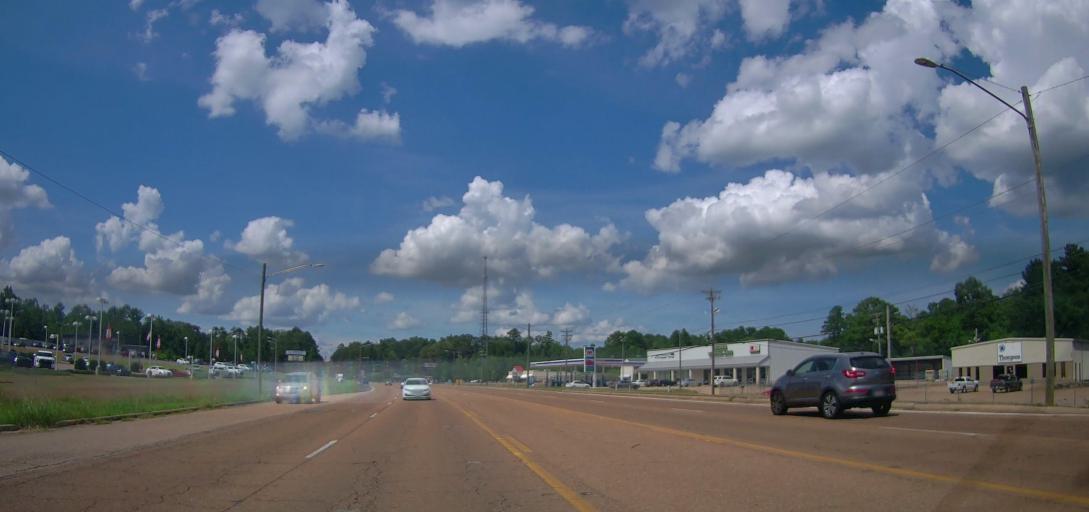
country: US
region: Mississippi
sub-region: Lowndes County
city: Columbus
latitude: 33.5490
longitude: -88.4335
